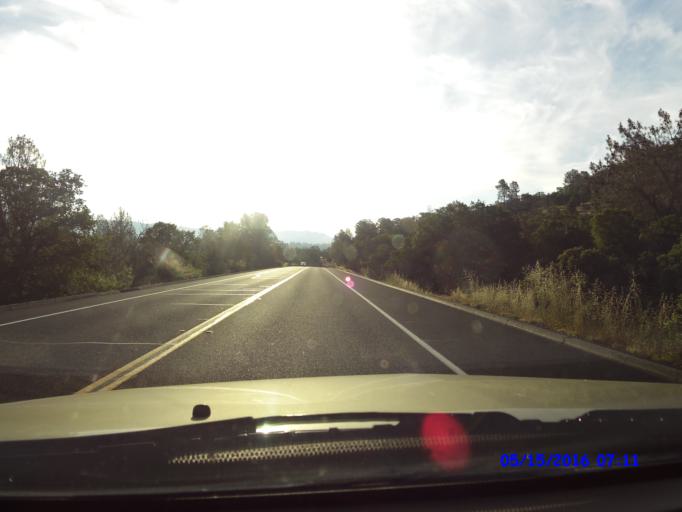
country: US
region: California
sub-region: Tuolumne County
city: Jamestown
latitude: 37.8502
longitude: -120.3979
